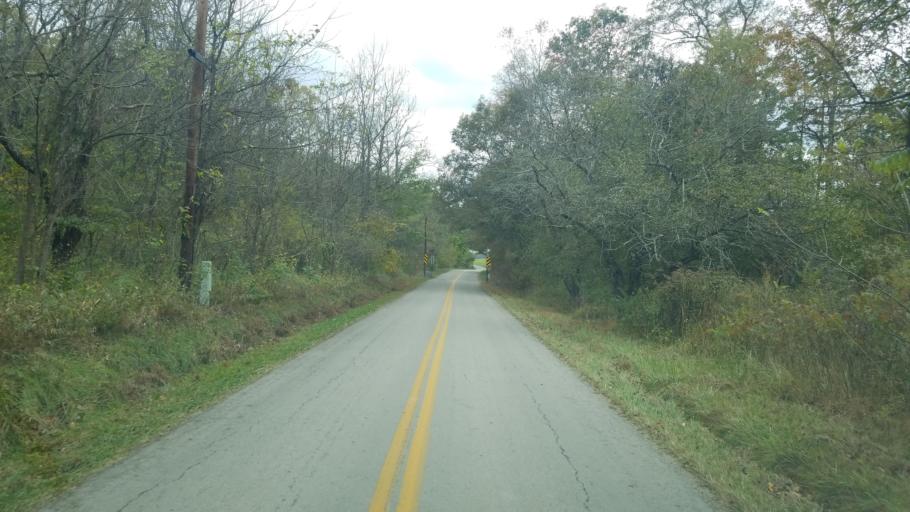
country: US
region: Ohio
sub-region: Jackson County
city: Jackson
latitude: 39.1623
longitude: -82.6466
